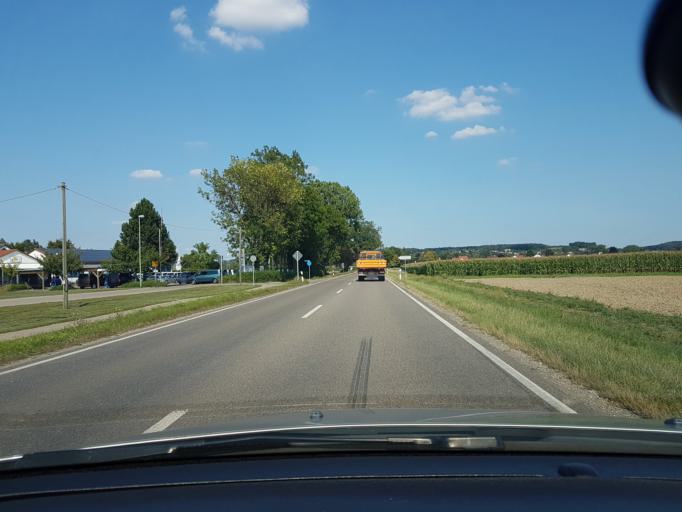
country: DE
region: Bavaria
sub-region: Swabia
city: Thierhaupten
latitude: 48.5641
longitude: 10.8875
